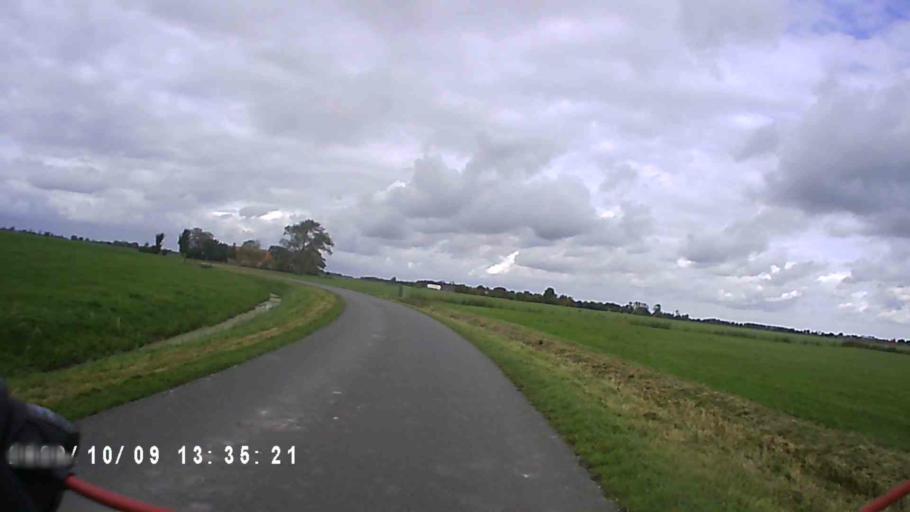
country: NL
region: Groningen
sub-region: Gemeente Zuidhorn
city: Aduard
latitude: 53.2954
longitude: 6.4715
